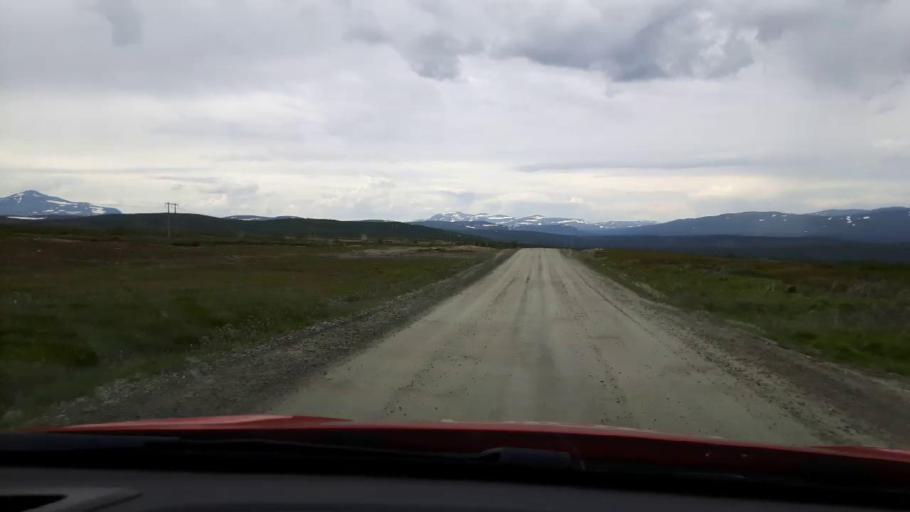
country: SE
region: Jaemtland
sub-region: Are Kommun
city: Are
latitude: 62.7714
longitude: 12.7666
